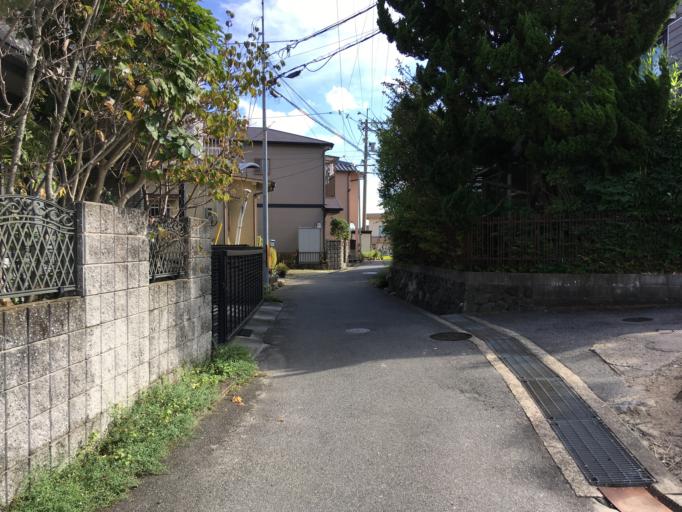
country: JP
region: Nara
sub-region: Ikoma-shi
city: Ikoma
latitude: 34.6718
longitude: 135.7062
